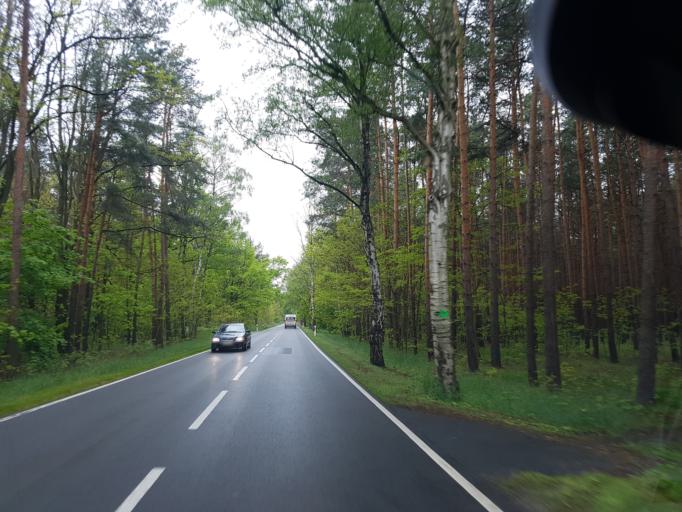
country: DE
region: Saxony
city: Schleife
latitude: 51.6096
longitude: 14.4820
